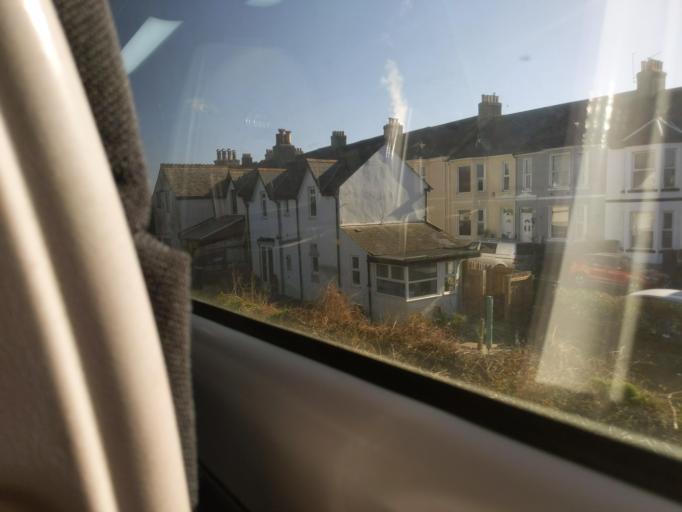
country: GB
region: England
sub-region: Cornwall
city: Torpoint
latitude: 50.4027
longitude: -4.1906
